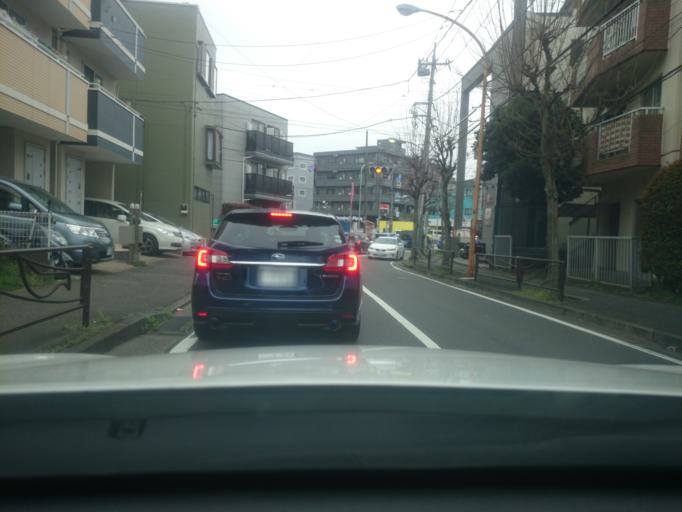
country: JP
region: Tokyo
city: Chofugaoka
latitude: 35.5754
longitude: 139.5710
